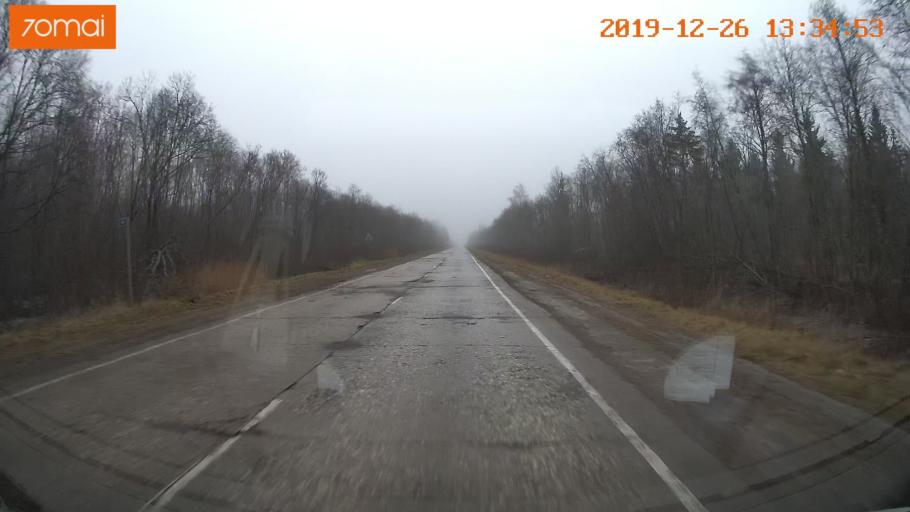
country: RU
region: Vologda
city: Sheksna
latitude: 58.8001
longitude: 38.3312
